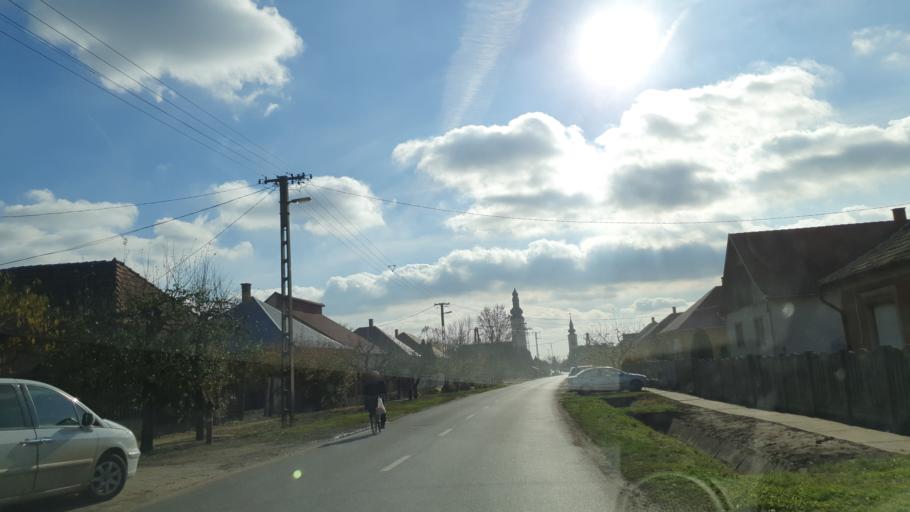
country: HU
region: Szabolcs-Szatmar-Bereg
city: Nyirkarasz
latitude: 48.1055
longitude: 22.0956
